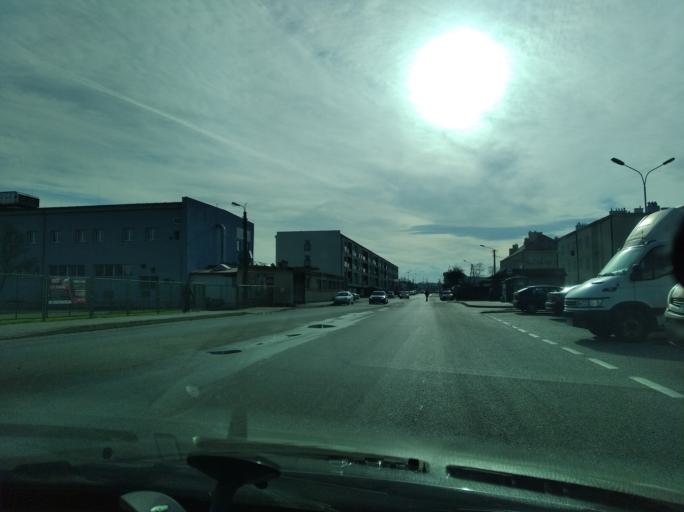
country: PL
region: Subcarpathian Voivodeship
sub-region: Powiat ropczycko-sedziszowski
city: Sedziszow Malopolski
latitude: 50.0723
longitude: 21.6900
